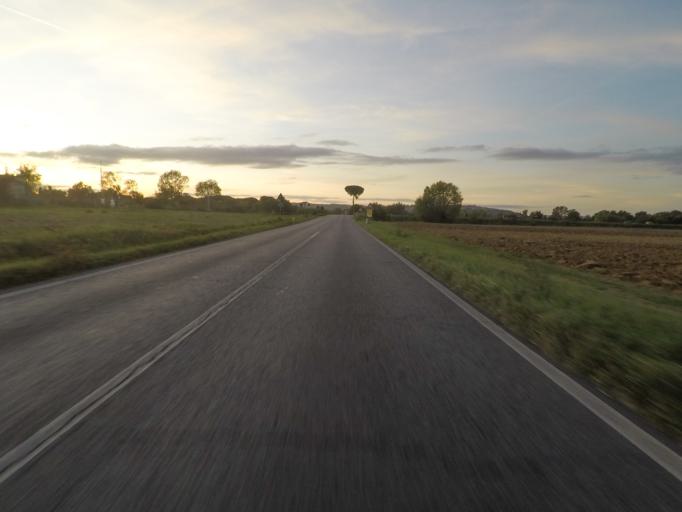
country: IT
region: Tuscany
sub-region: Provincia di Siena
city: Sinalunga
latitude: 43.1889
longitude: 11.7589
